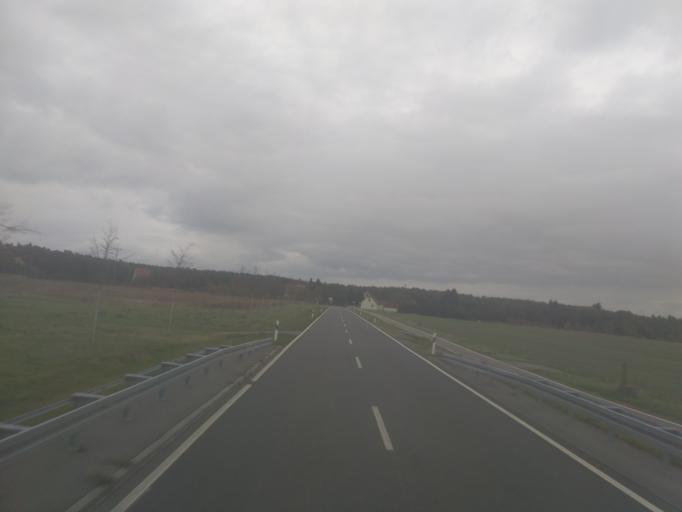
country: DE
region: Brandenburg
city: Merzdorf
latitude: 51.3861
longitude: 13.5064
